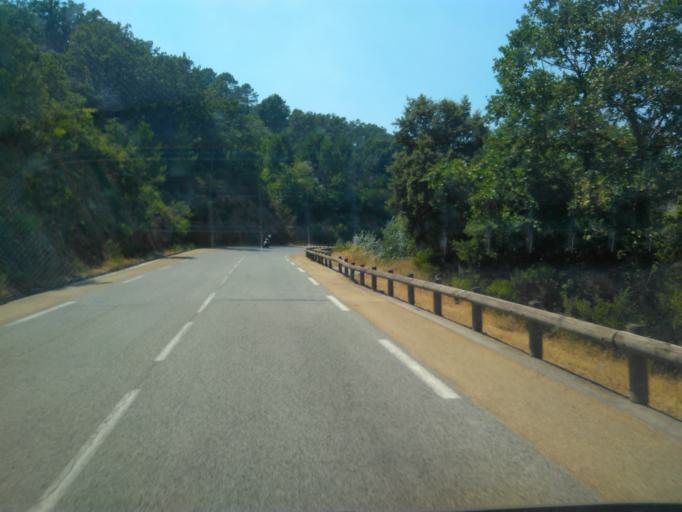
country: FR
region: Provence-Alpes-Cote d'Azur
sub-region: Departement du Var
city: La Garde-Freinet
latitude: 43.3021
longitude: 6.4860
